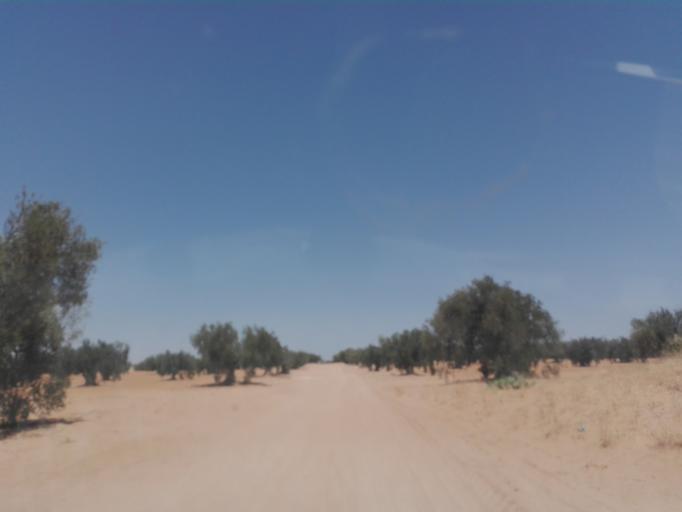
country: TN
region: Safaqis
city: Bi'r `Ali Bin Khalifah
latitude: 34.6495
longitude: 10.2724
